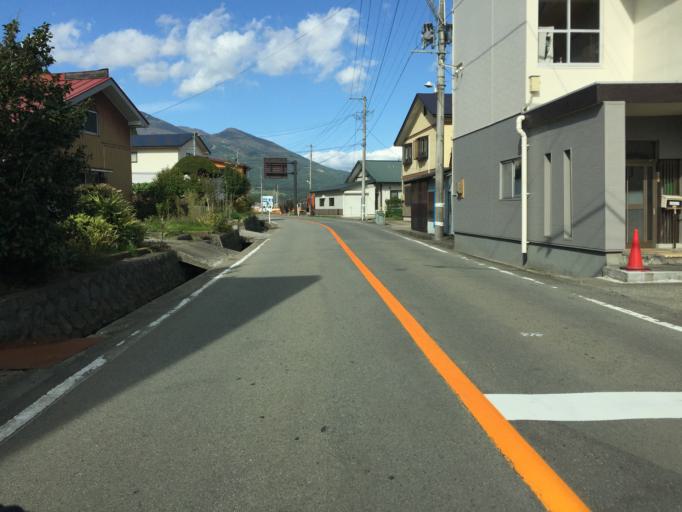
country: JP
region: Fukushima
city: Inawashiro
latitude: 37.5369
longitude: 140.0621
